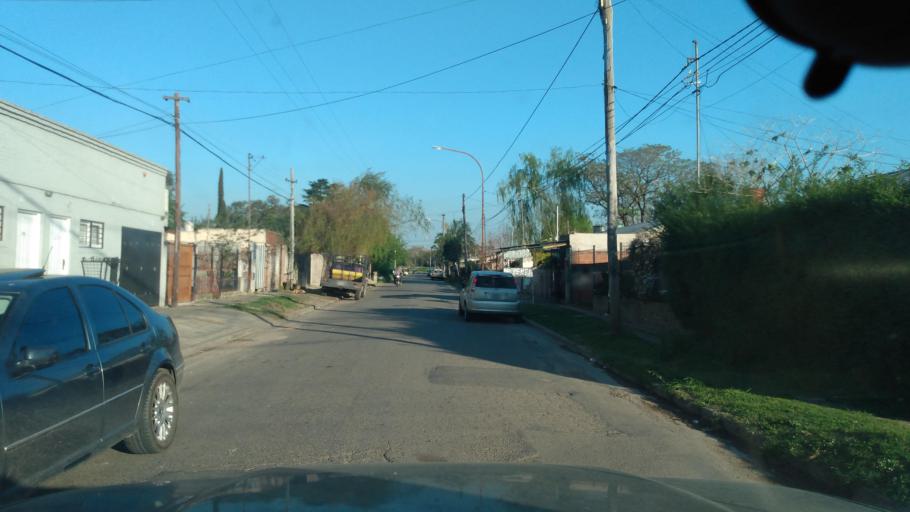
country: AR
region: Buenos Aires
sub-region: Partido de Lujan
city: Lujan
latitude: -34.5784
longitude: -59.1154
